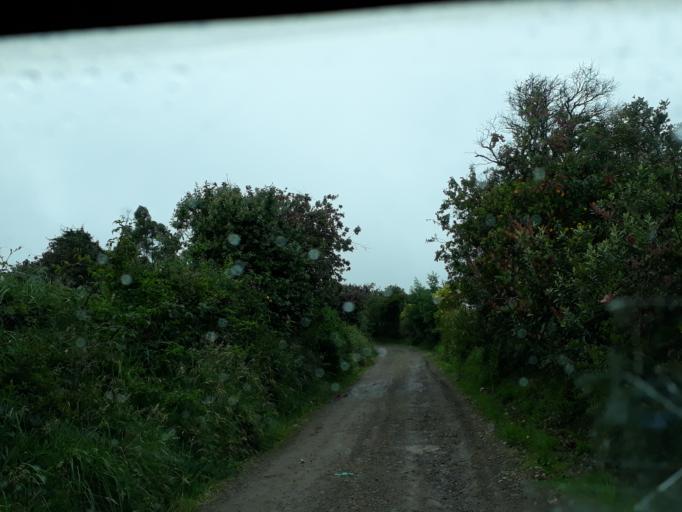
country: CO
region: Cundinamarca
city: Sutatausa
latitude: 5.1567
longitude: -73.9052
